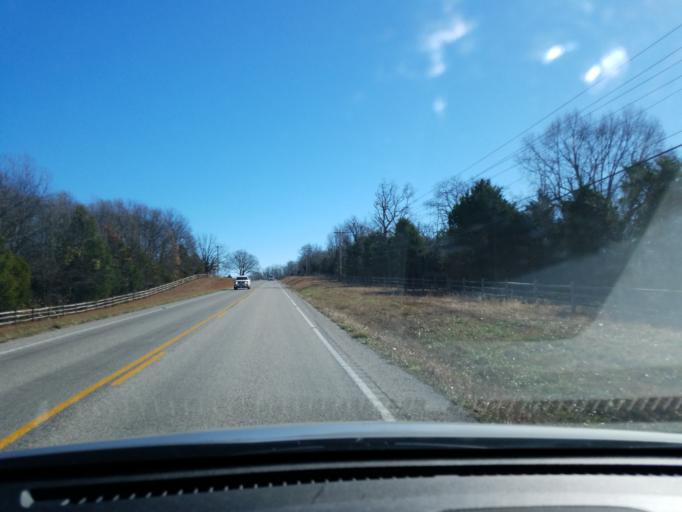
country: US
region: Missouri
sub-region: Taney County
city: Hollister
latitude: 36.5221
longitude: -93.2717
